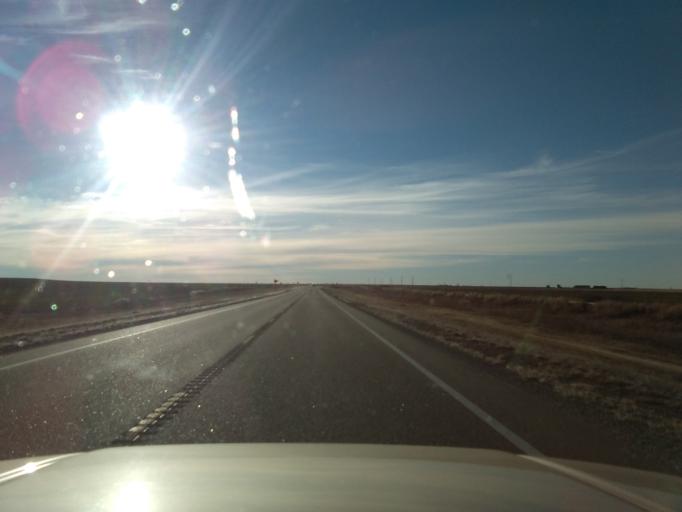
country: US
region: Kansas
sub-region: Sheridan County
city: Hoxie
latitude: 39.5125
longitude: -100.6410
